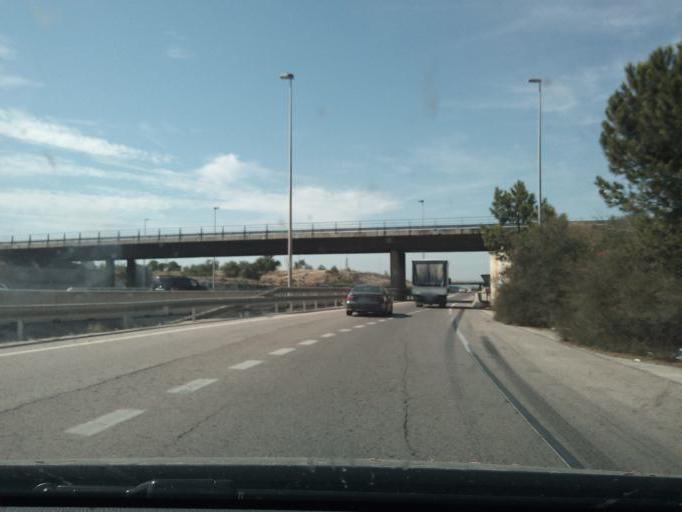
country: ES
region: Valencia
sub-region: Provincia de Valencia
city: Godella
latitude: 39.5390
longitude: -0.4548
